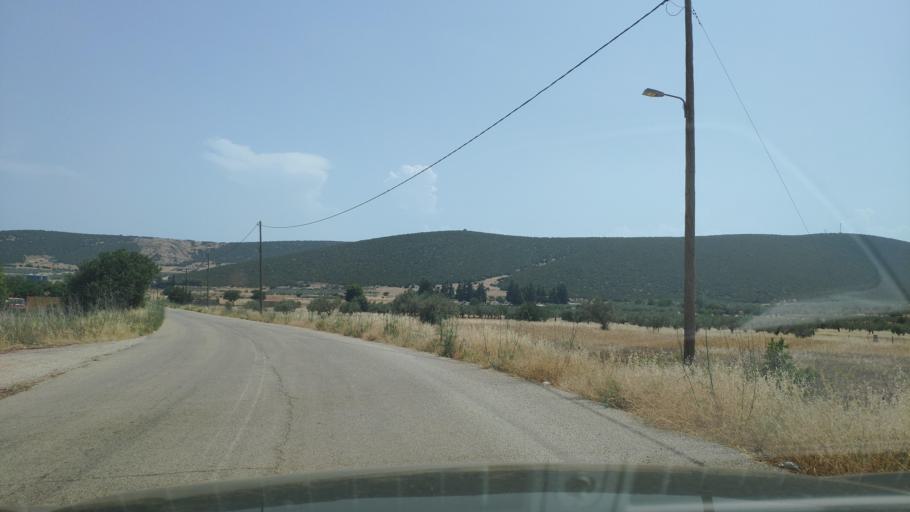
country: GR
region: Peloponnese
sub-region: Nomos Argolidos
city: Didyma
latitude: 37.4644
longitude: 23.1683
